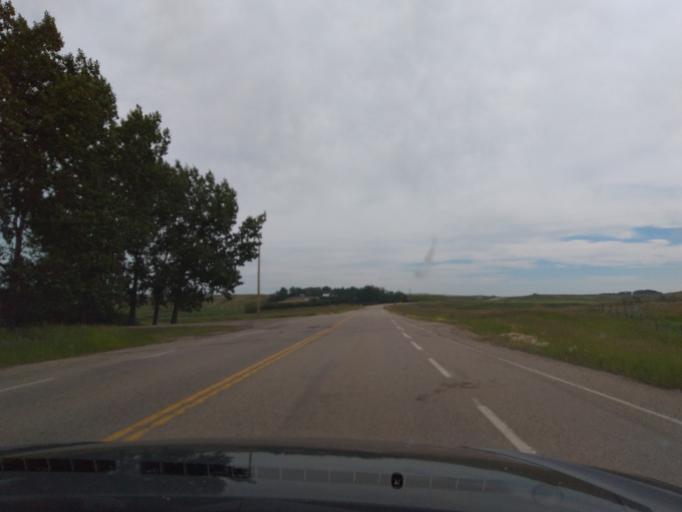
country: CA
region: Alberta
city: Three Hills
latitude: 51.5021
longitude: -113.3343
